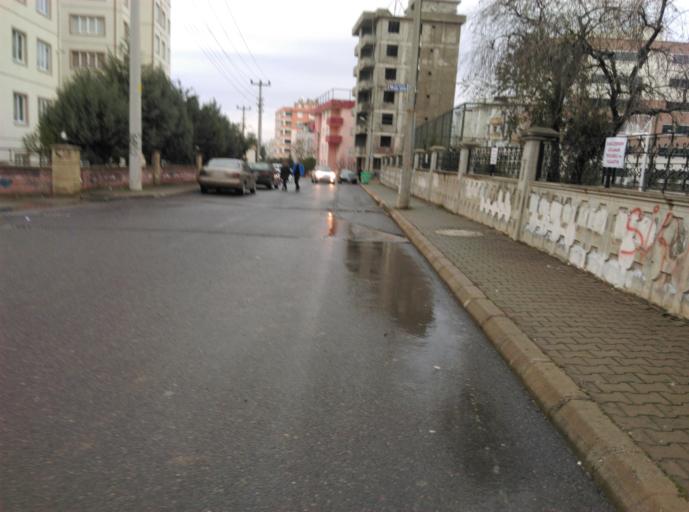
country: TR
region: Kahramanmaras
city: Kahramanmaras
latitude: 37.5821
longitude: 36.8942
